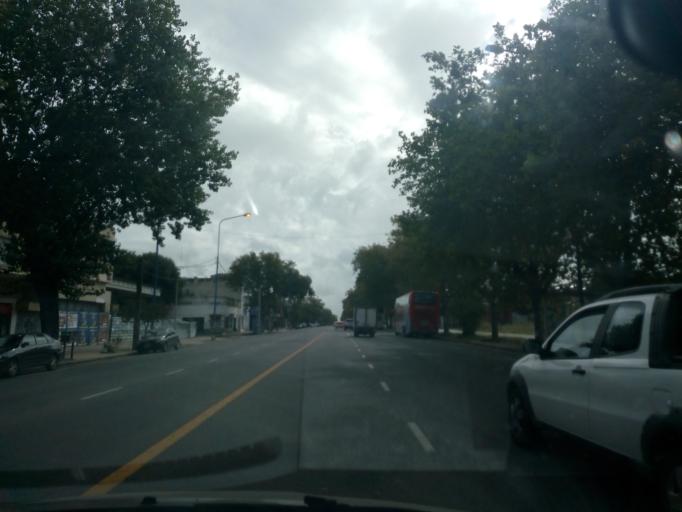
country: AR
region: Buenos Aires
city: Mar del Plata
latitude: -37.9893
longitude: -57.5644
